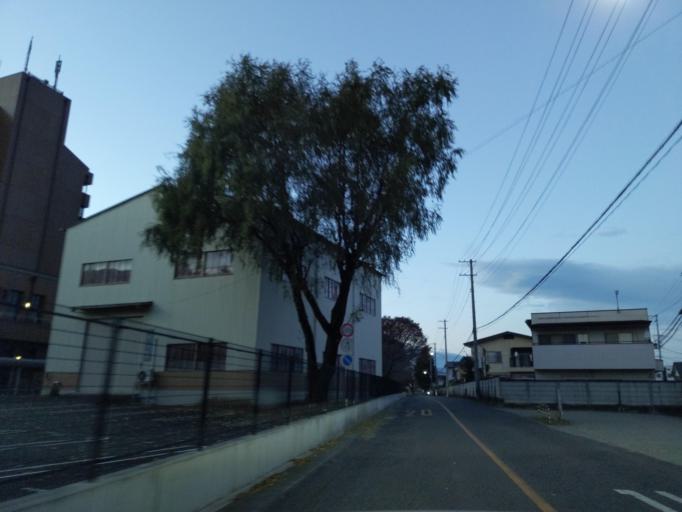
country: JP
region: Fukushima
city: Koriyama
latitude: 37.3602
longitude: 140.3838
